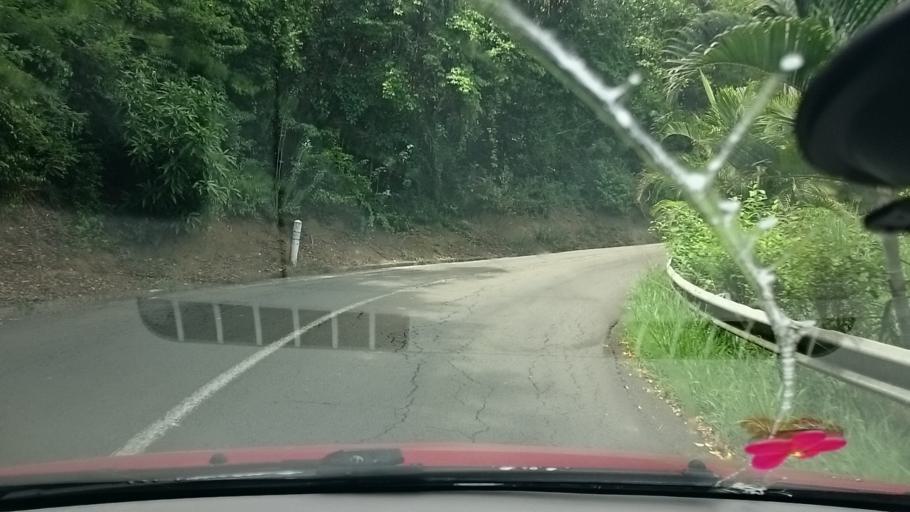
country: MQ
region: Martinique
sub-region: Martinique
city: La Trinite
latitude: 14.7555
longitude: -60.9225
